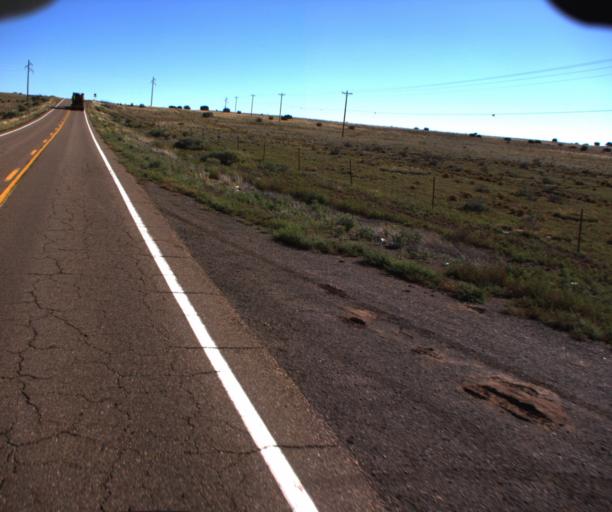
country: US
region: Arizona
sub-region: Apache County
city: Saint Johns
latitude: 34.4929
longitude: -109.5144
